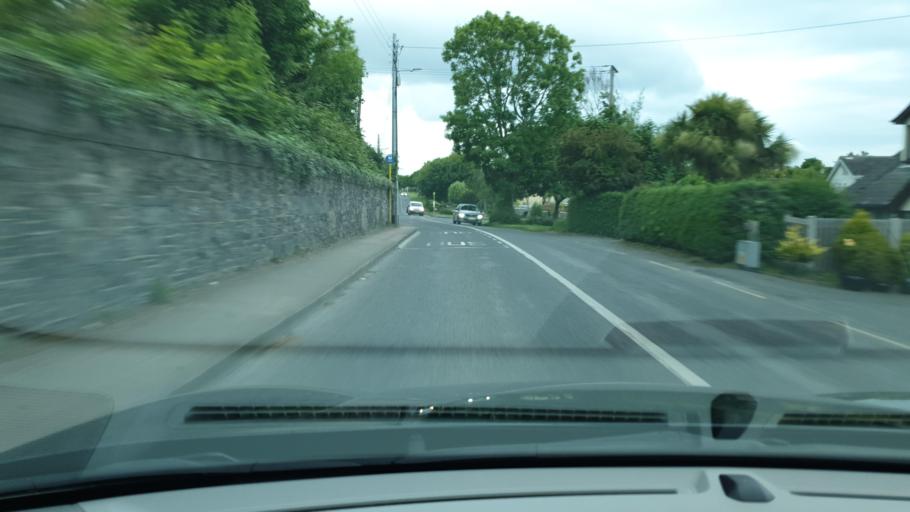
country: IE
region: Leinster
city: Balbriggan
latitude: 53.6027
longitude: -6.1673
